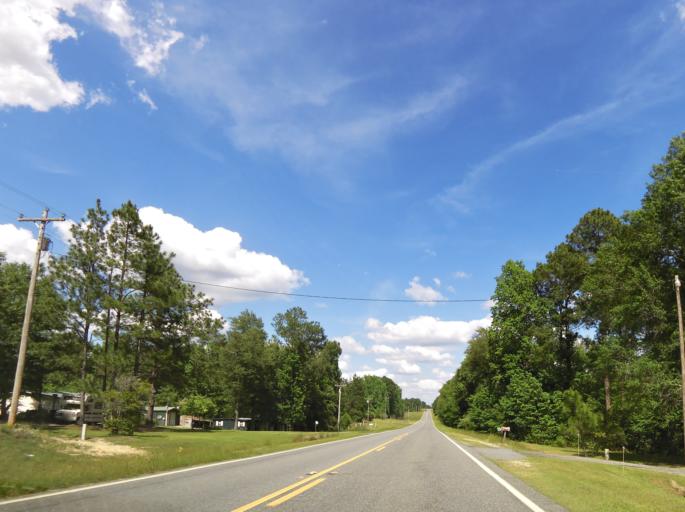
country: US
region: Georgia
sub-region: Wheeler County
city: Alamo
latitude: 32.2500
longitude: -82.9171
